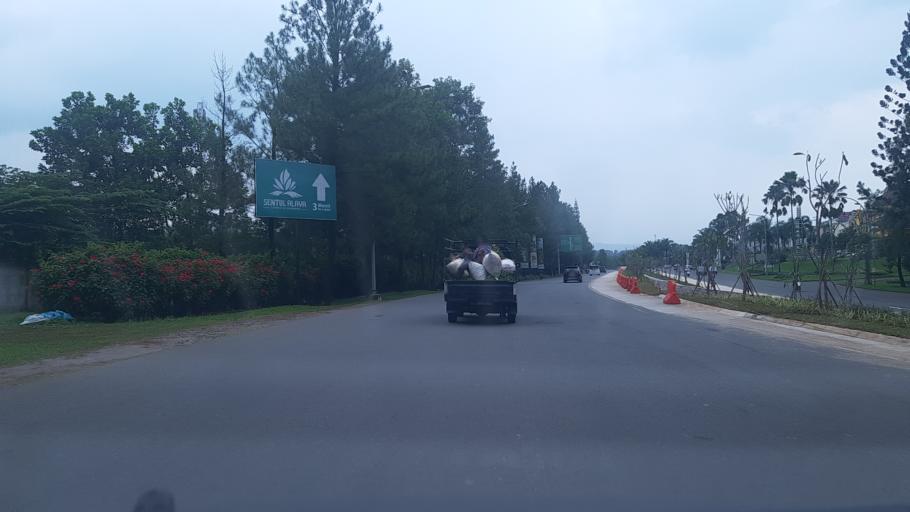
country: ID
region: West Java
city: Bogor
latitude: -6.5690
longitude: 106.8613
